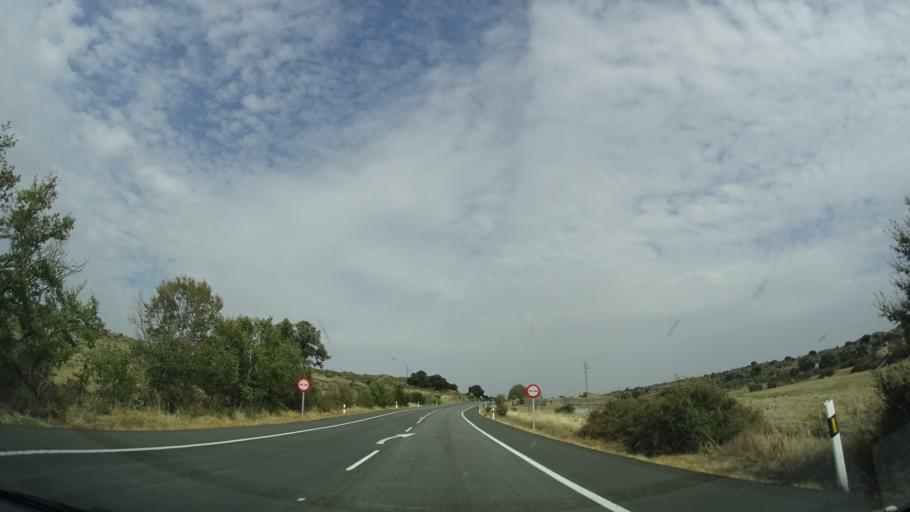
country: ES
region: Extremadura
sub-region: Provincia de Caceres
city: Trujillo
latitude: 39.4381
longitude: -5.8890
